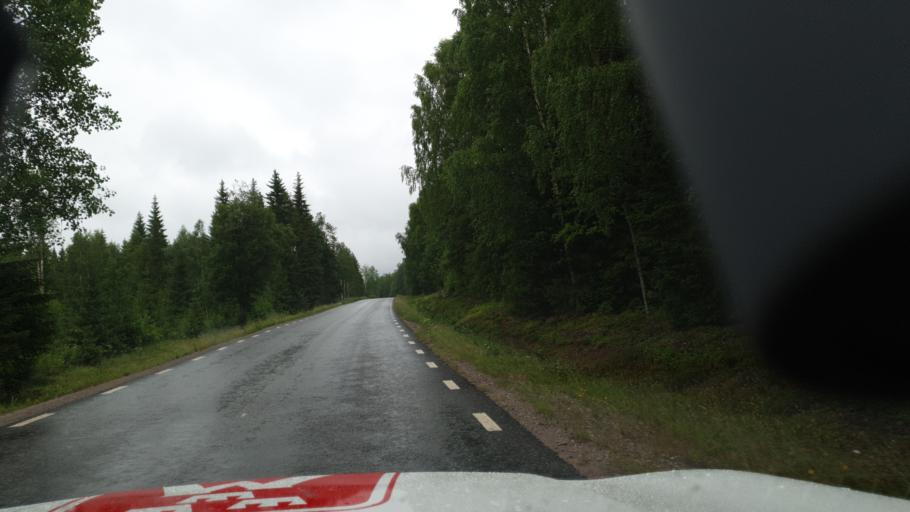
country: SE
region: Vaesterbotten
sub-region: Vannas Kommun
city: Vannasby
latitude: 63.8051
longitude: 19.8519
